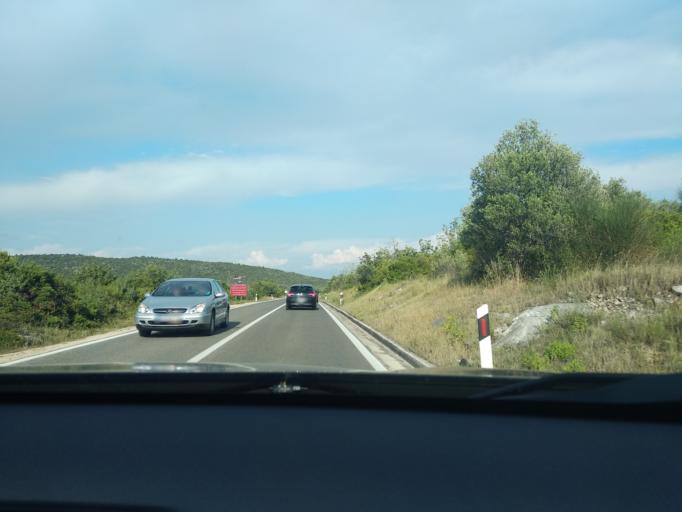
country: HR
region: Sibensko-Kniniska
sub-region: Grad Sibenik
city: Pirovac
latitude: 43.7976
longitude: 15.6825
